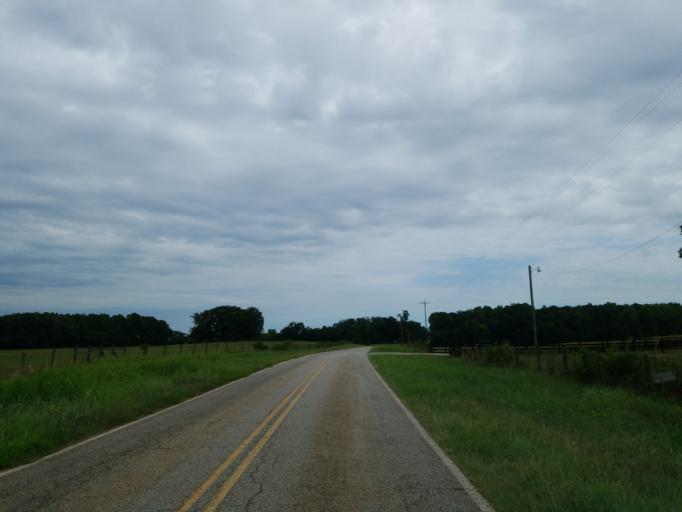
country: US
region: Georgia
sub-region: Monroe County
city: Forsyth
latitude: 32.9941
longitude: -84.0469
